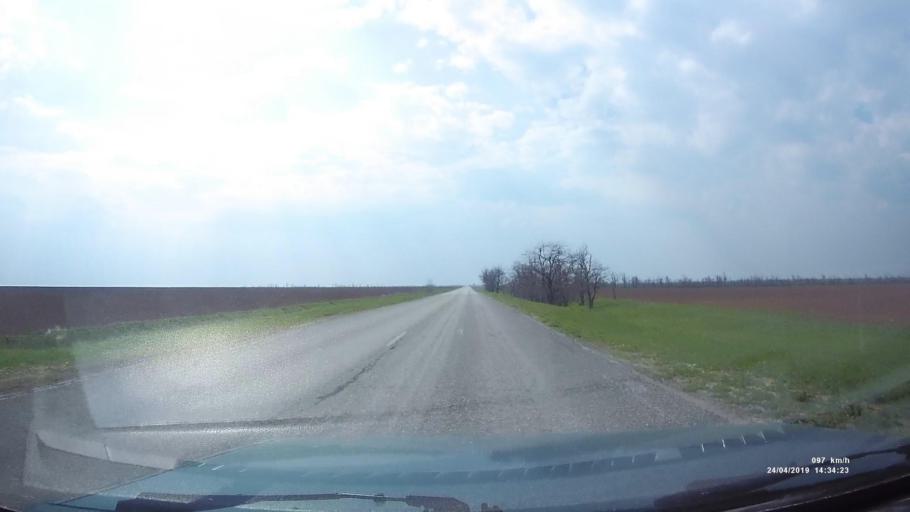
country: RU
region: Kalmykiya
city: Arshan'
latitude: 46.3737
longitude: 43.9328
